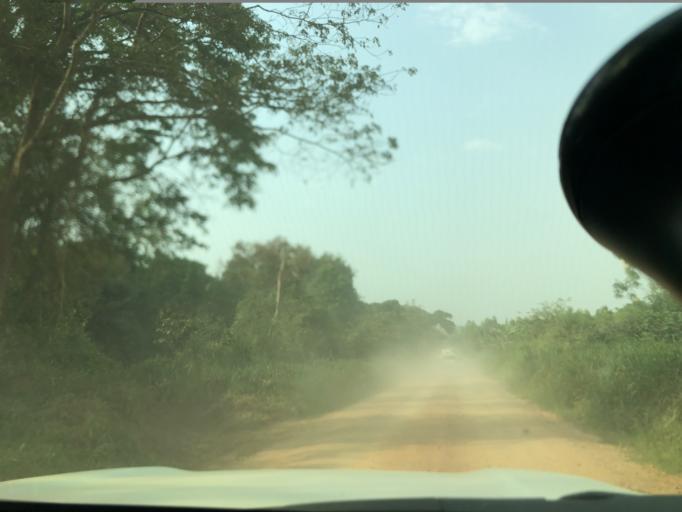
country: UG
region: Western Region
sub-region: Kasese District
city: Margherita
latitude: 0.1801
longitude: 29.6589
